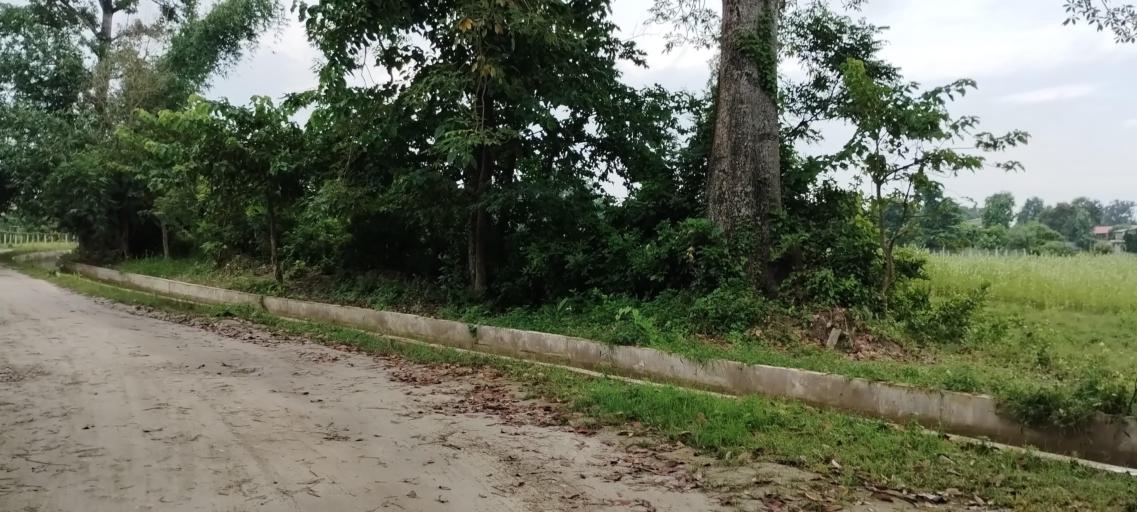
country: NP
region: Far Western
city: Tikapur
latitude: 28.4510
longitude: 81.2419
